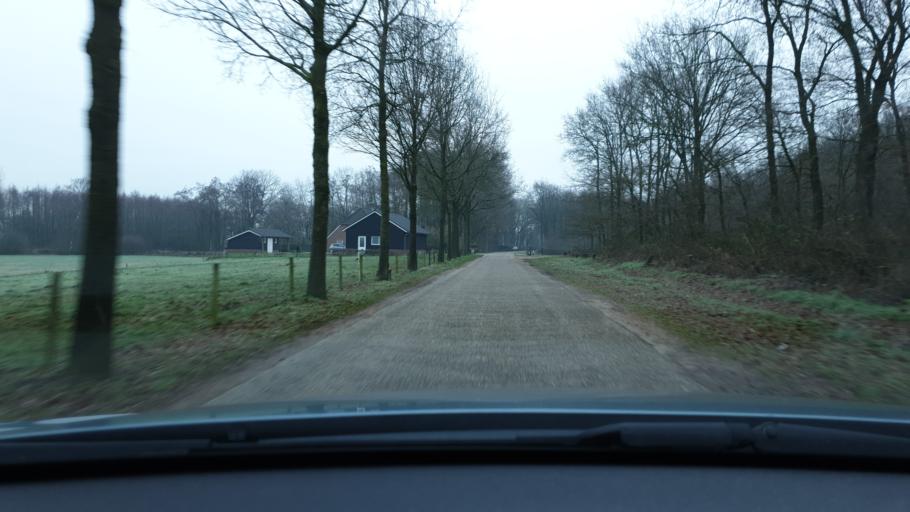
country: NL
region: Gelderland
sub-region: Gemeente Wijchen
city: Bergharen
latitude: 51.8620
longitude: 5.6708
